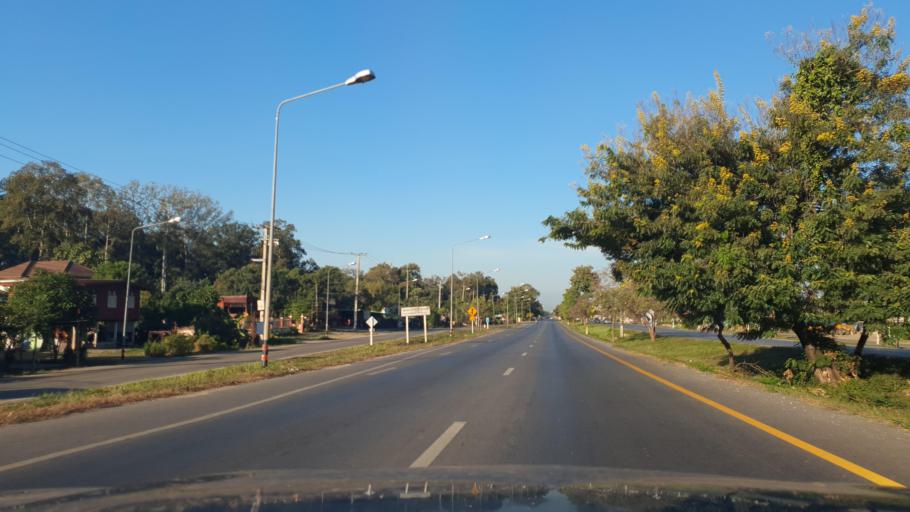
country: TH
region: Phitsanulok
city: Phitsanulok
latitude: 16.8648
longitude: 100.2432
